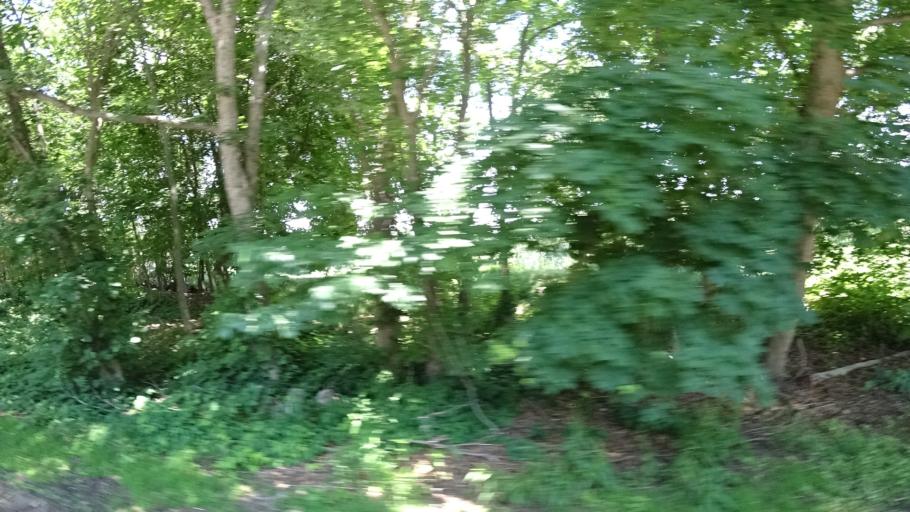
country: US
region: Massachusetts
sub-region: Norfolk County
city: Needham
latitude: 42.2510
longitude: -71.2239
